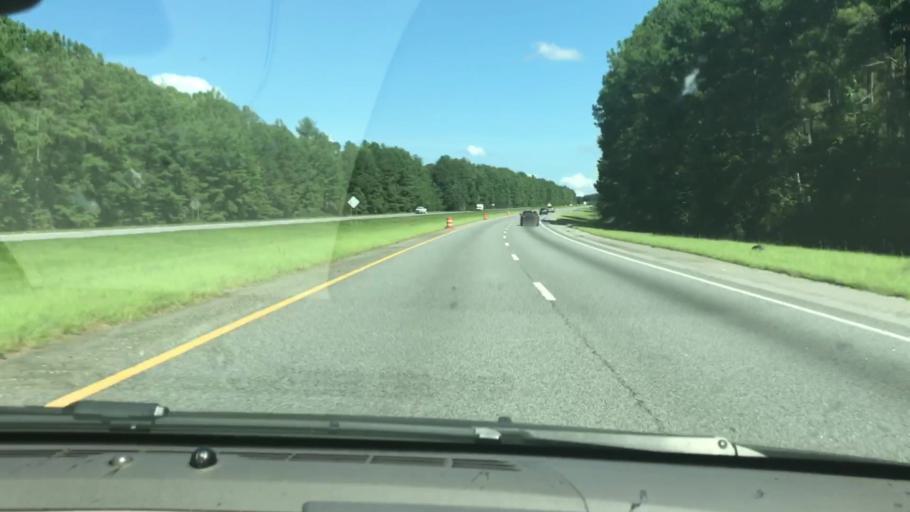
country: US
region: Georgia
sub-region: Harris County
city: Hamilton
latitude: 32.6386
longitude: -84.9686
